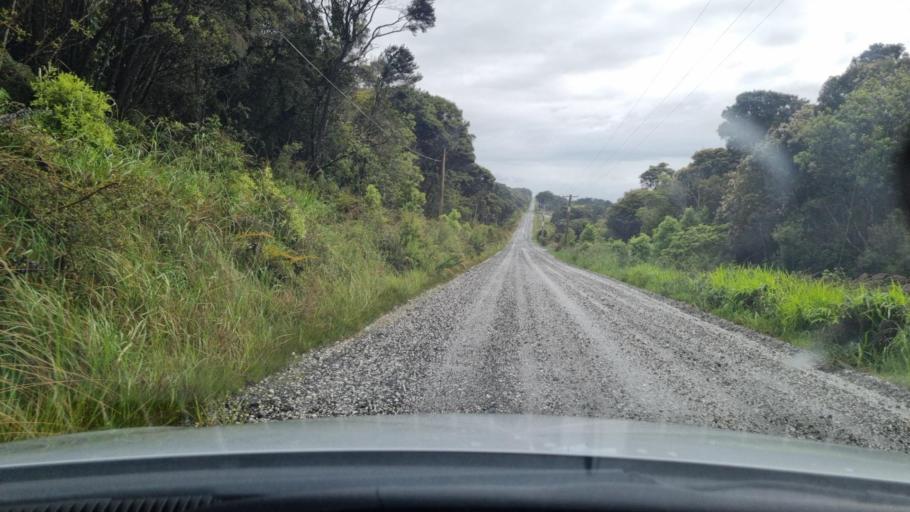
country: NZ
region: Southland
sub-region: Invercargill City
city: Bluff
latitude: -46.5396
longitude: 168.2643
